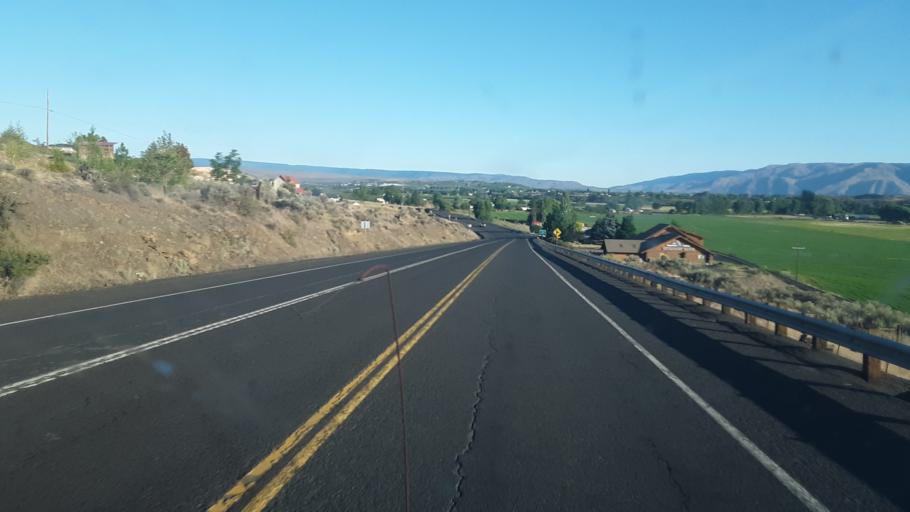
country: US
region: Washington
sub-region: Yakima County
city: Gleed
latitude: 46.6332
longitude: -120.6746
